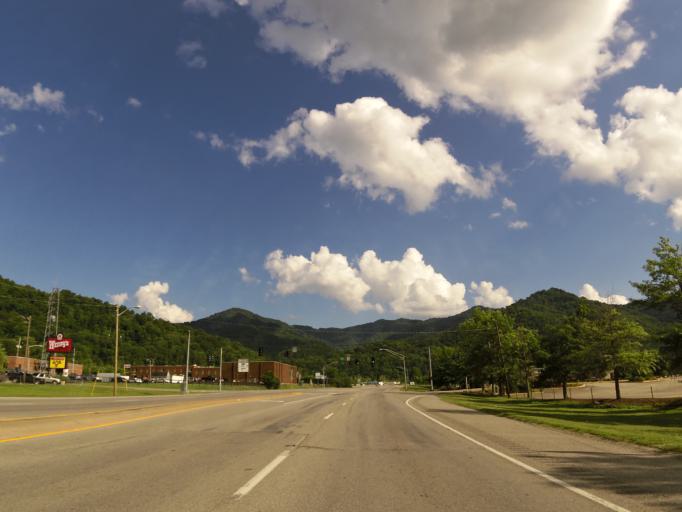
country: US
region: Kentucky
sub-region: Harlan County
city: Harlan
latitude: 36.8160
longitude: -83.3154
